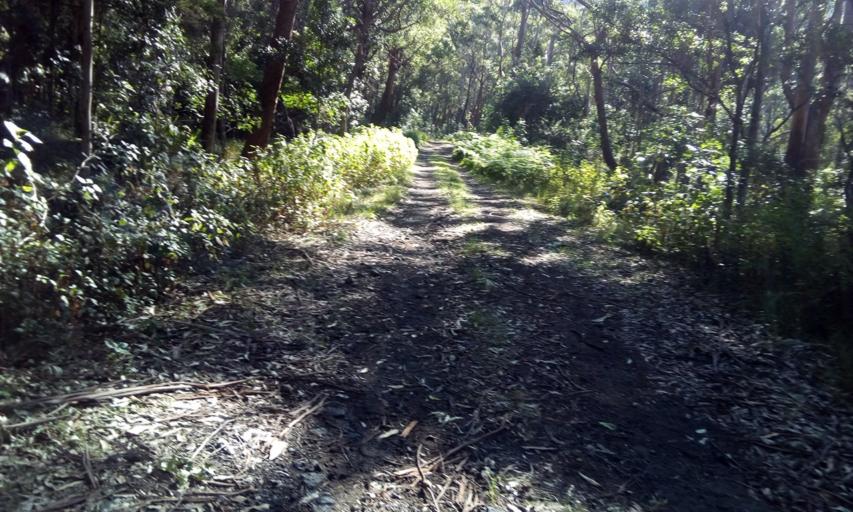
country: AU
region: New South Wales
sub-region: Wollongong
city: Cordeaux Heights
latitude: -34.4358
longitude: 150.8064
